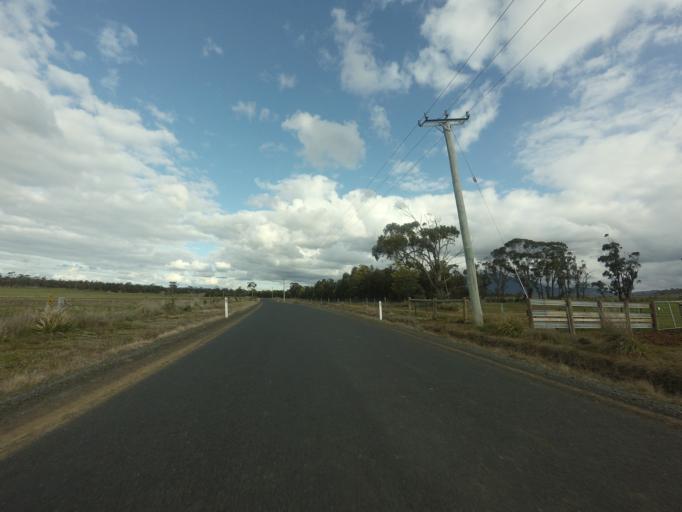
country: AU
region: Tasmania
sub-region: Northern Midlands
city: Longford
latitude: -41.8321
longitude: 147.2068
